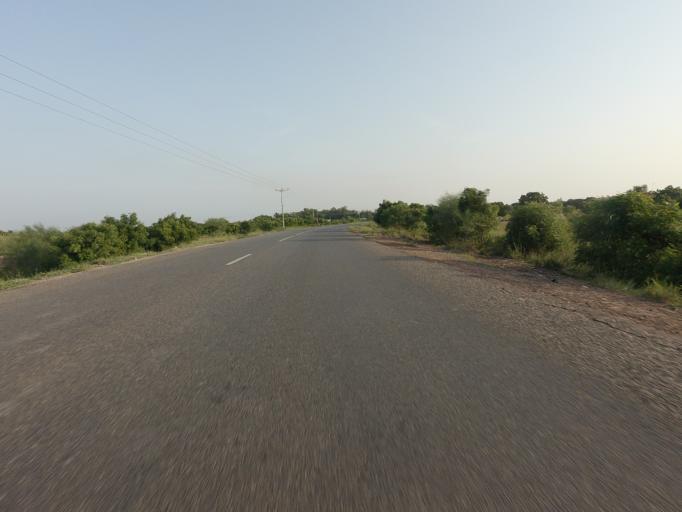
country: GH
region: Volta
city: Anloga
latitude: 5.9737
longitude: 0.6660
